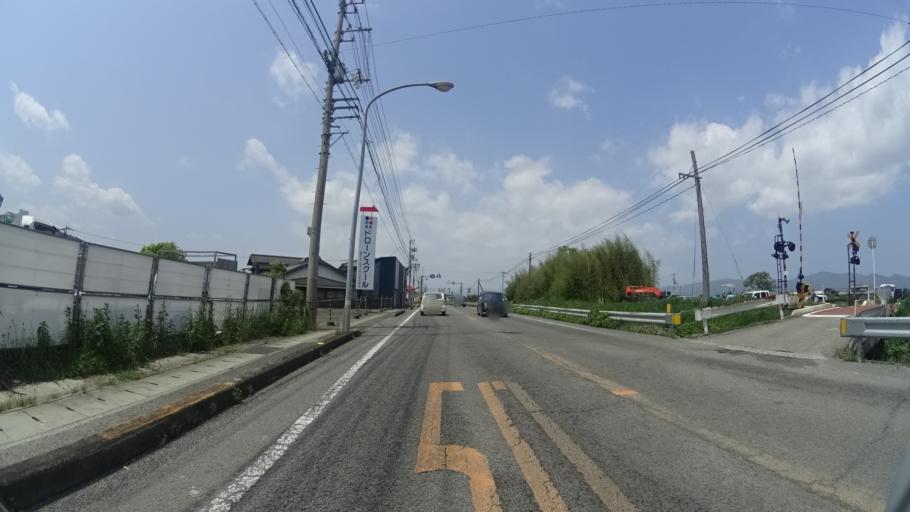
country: JP
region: Tokushima
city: Ishii
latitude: 34.0661
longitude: 134.4286
